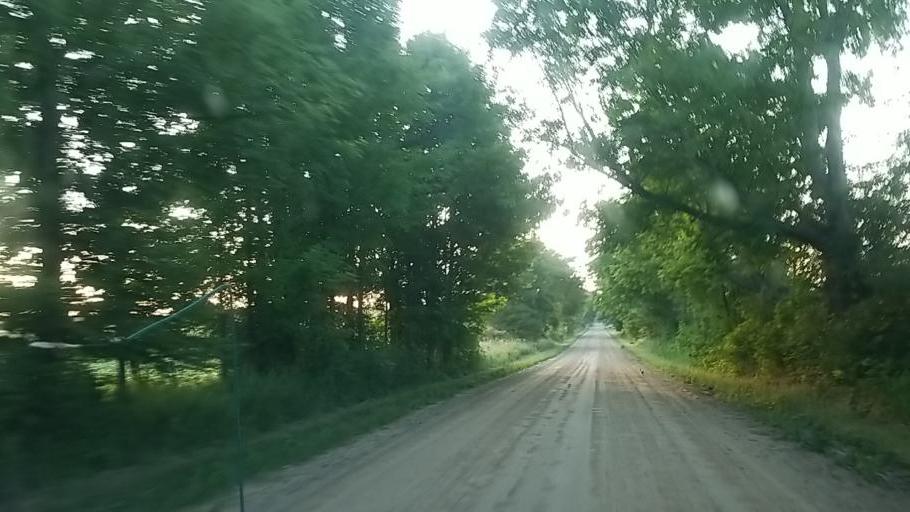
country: US
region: Michigan
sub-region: Osceola County
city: Evart
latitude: 43.9151
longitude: -85.1859
